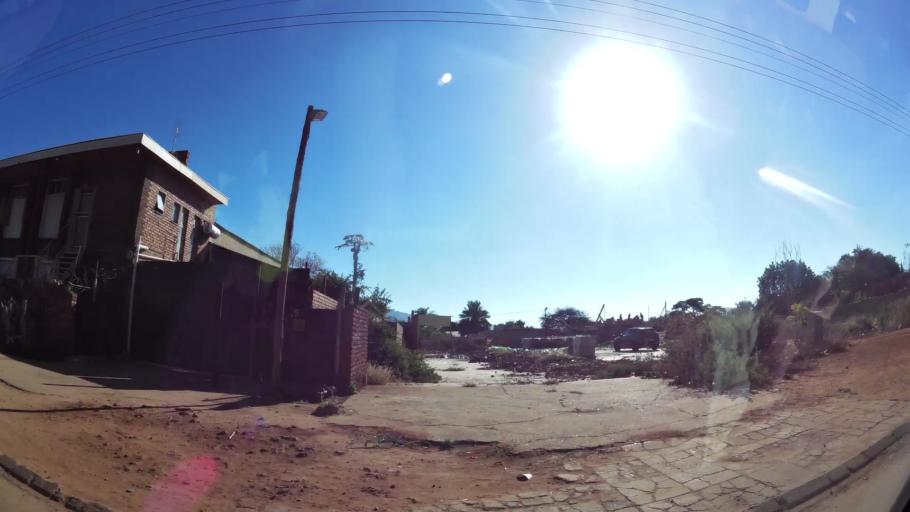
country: ZA
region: Limpopo
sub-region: Waterberg District Municipality
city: Mokopane
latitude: -24.1786
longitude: 28.9943
